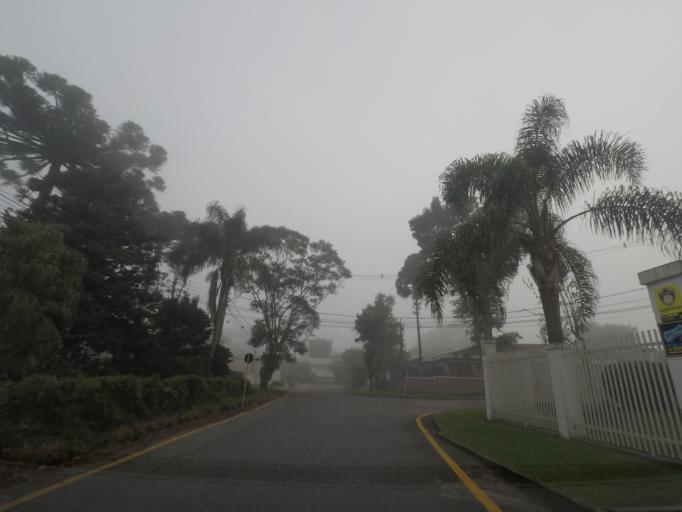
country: BR
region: Parana
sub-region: Curitiba
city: Curitiba
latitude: -25.4451
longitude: -49.2972
